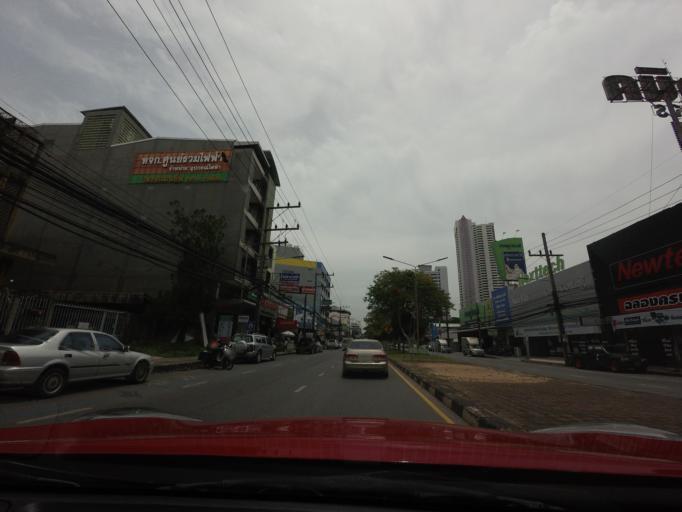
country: TH
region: Songkhla
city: Hat Yai
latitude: 6.9982
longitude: 100.4833
